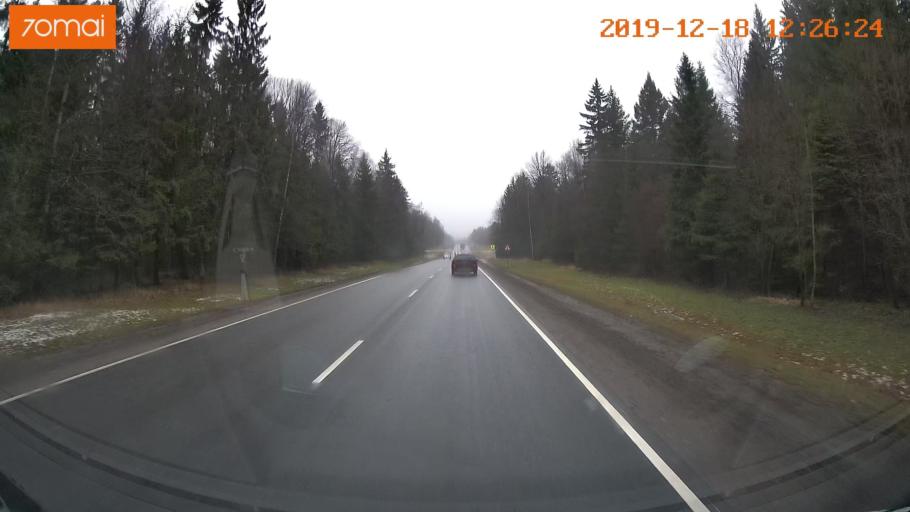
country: RU
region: Moskovskaya
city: Novopetrovskoye
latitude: 56.0508
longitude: 36.5010
